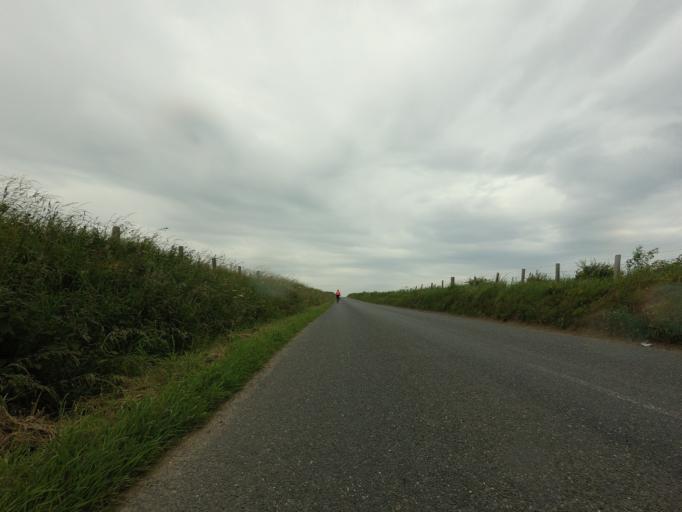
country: GB
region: Scotland
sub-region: Aberdeenshire
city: Whitehills
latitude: 57.6704
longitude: -2.6132
